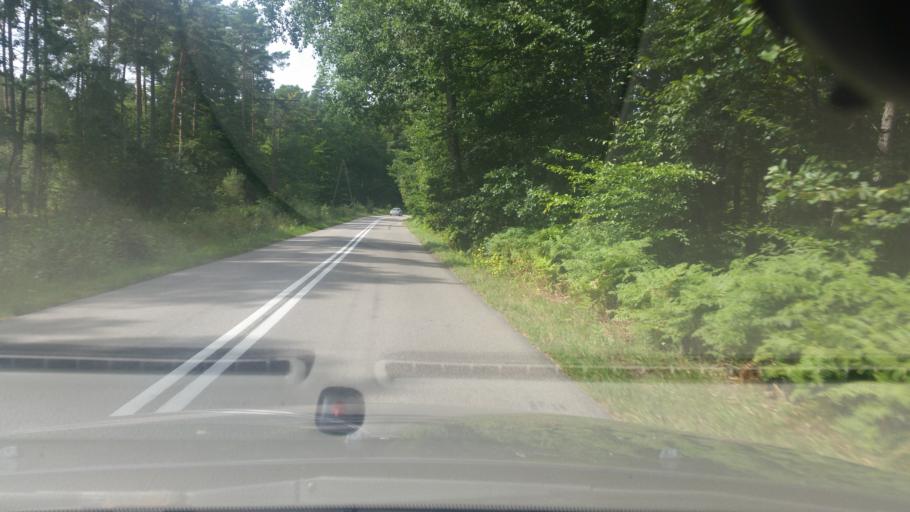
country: PL
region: Pomeranian Voivodeship
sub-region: Powiat wejherowski
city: Choczewo
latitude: 54.7458
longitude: 17.7402
